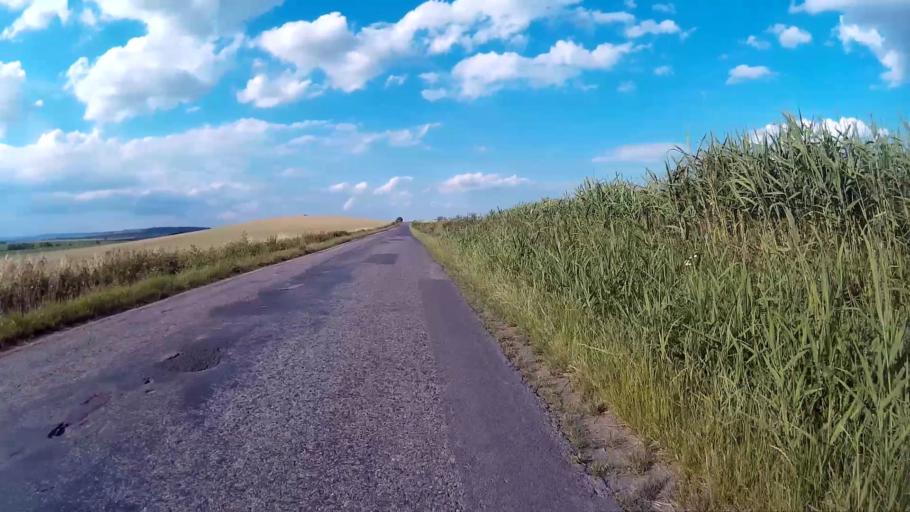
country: CZ
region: South Moravian
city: Tesany
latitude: 49.0554
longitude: 16.7786
